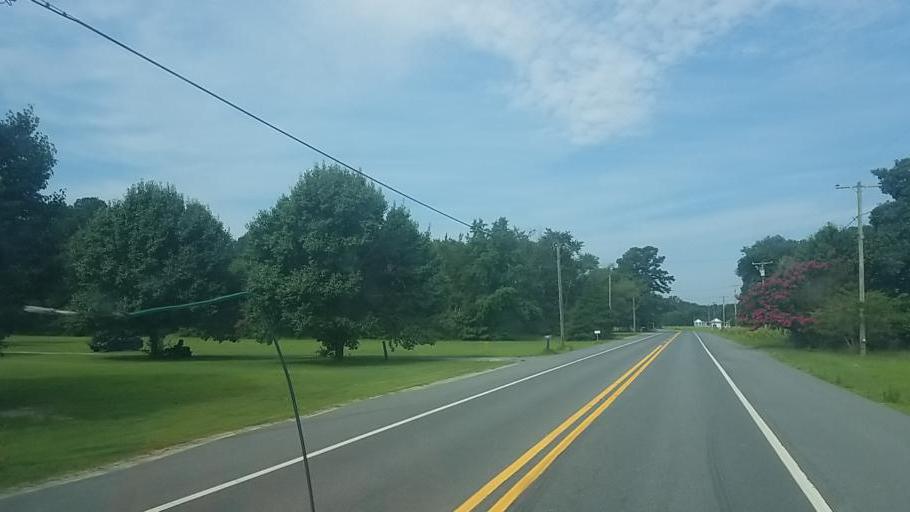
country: US
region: Delaware
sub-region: Sussex County
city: Ocean View
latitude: 38.5480
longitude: -75.1532
